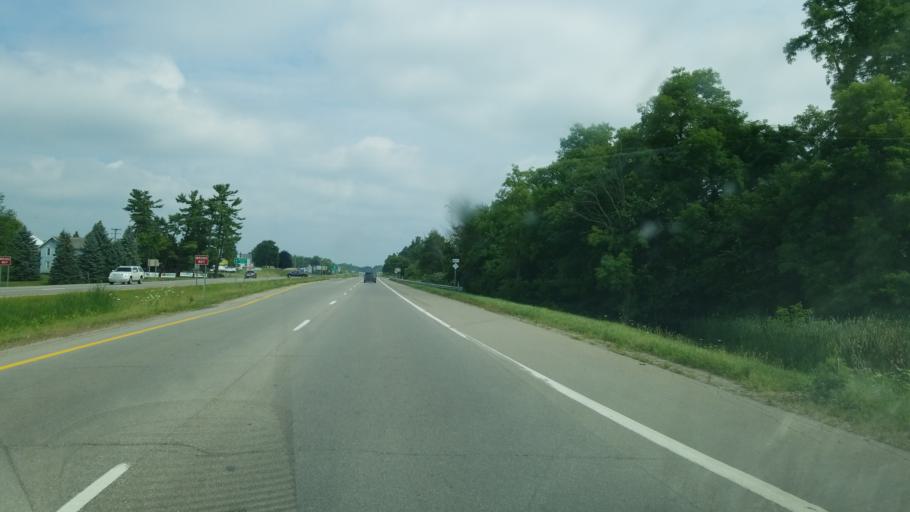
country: US
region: Michigan
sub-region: Kent County
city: Comstock Park
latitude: 43.0730
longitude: -85.6899
